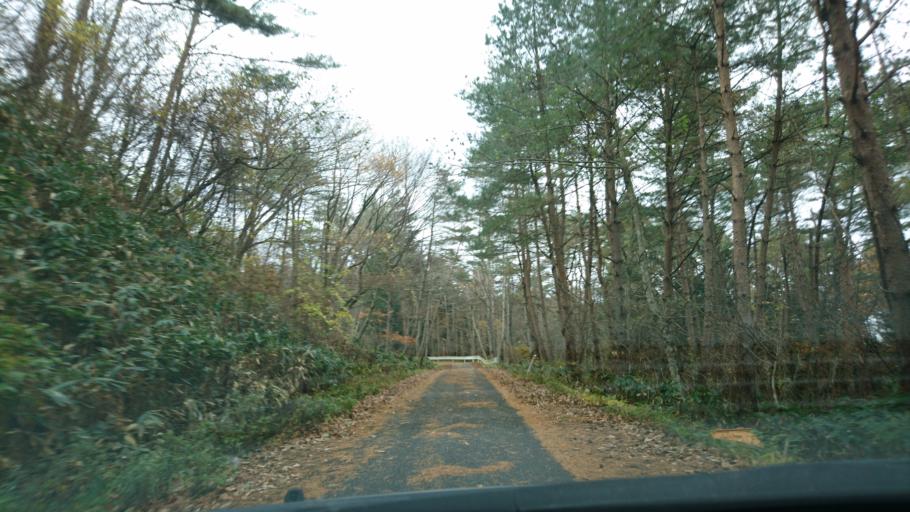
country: JP
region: Iwate
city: Ichinoseki
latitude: 39.0025
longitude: 141.1950
